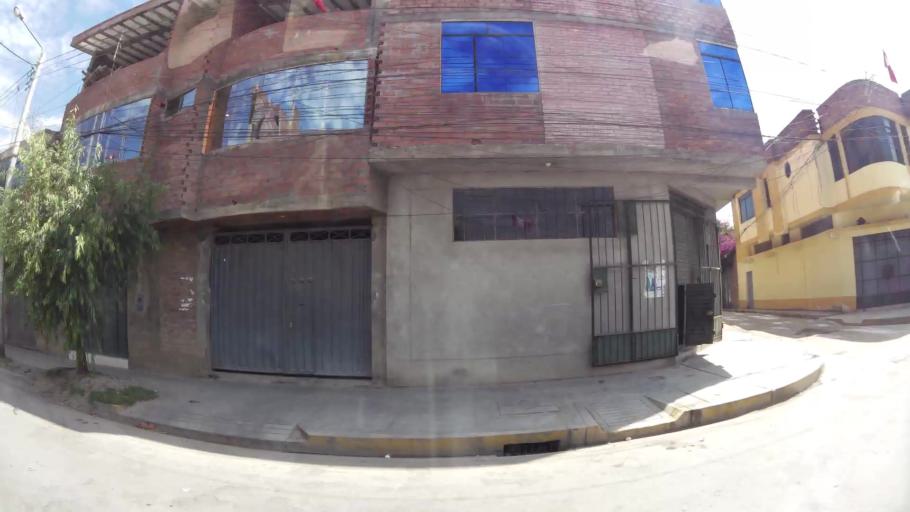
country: PE
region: Junin
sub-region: Provincia de Huancayo
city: El Tambo
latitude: -12.0755
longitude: -75.2161
